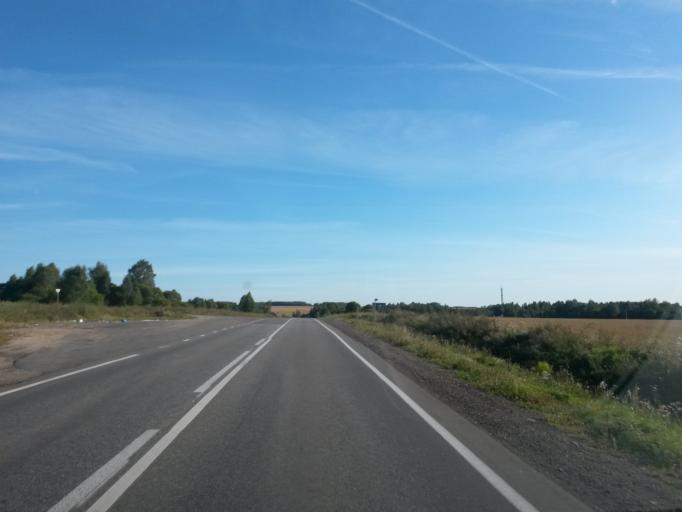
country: RU
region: Jaroslavl
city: Gavrilov-Yam
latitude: 57.3336
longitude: 39.9207
